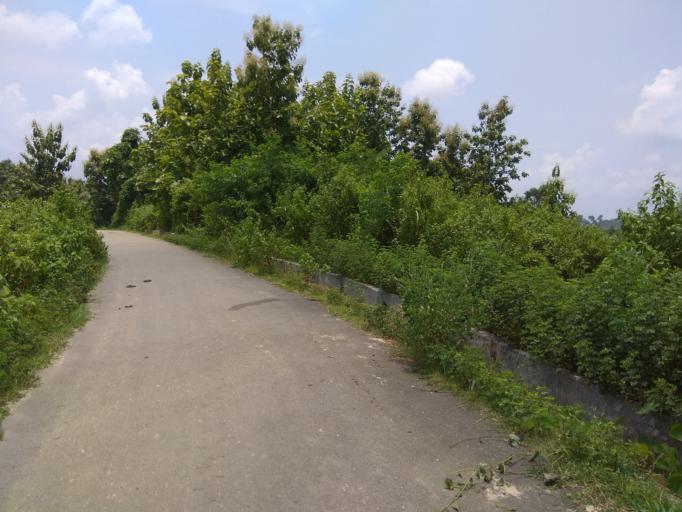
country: BD
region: Chittagong
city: Manikchari
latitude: 22.8896
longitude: 91.9224
